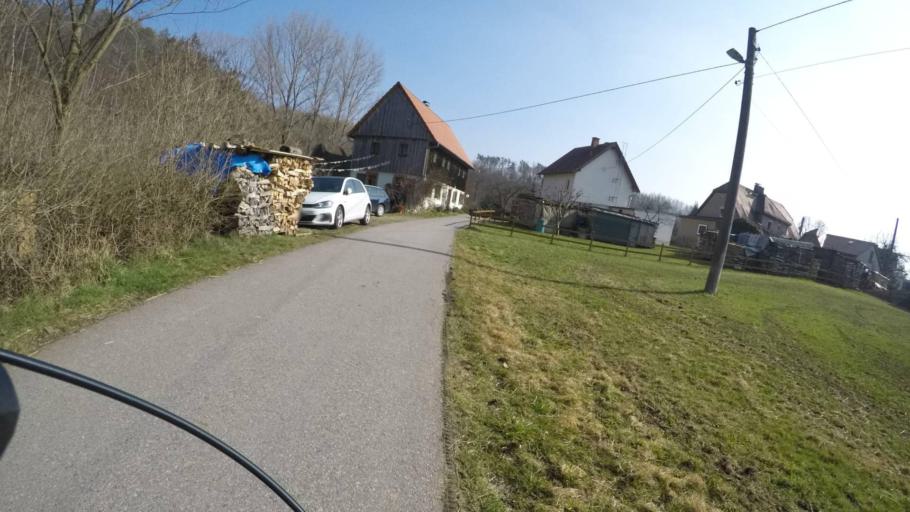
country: DE
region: Saxony
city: Niederfrohna
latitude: 50.9038
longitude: 12.6778
